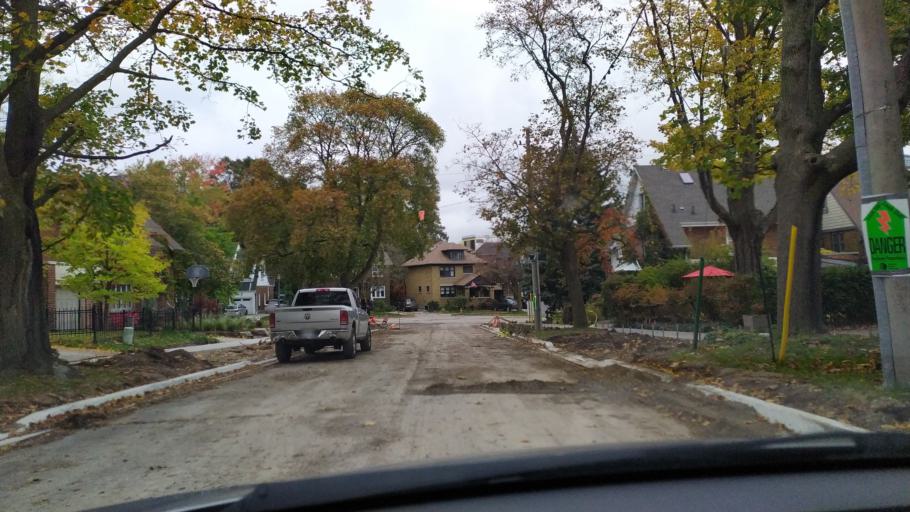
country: CA
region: Ontario
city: Waterloo
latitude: 43.4541
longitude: -80.5203
